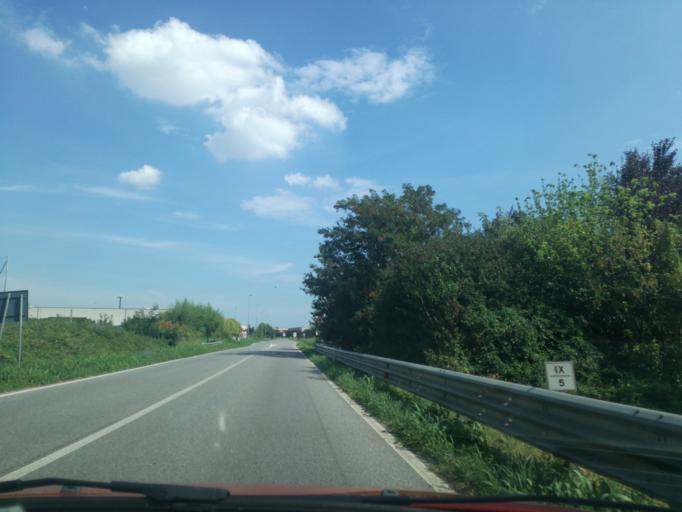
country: IT
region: Lombardy
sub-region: Citta metropolitana di Milano
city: Grezzago
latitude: 45.5868
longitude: 9.4941
